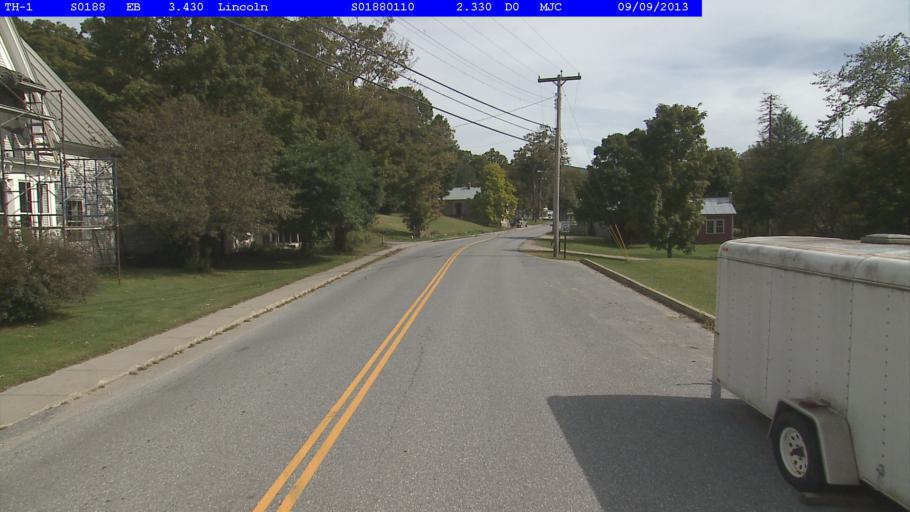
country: US
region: Vermont
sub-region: Addison County
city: Bristol
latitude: 44.1054
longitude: -72.9960
